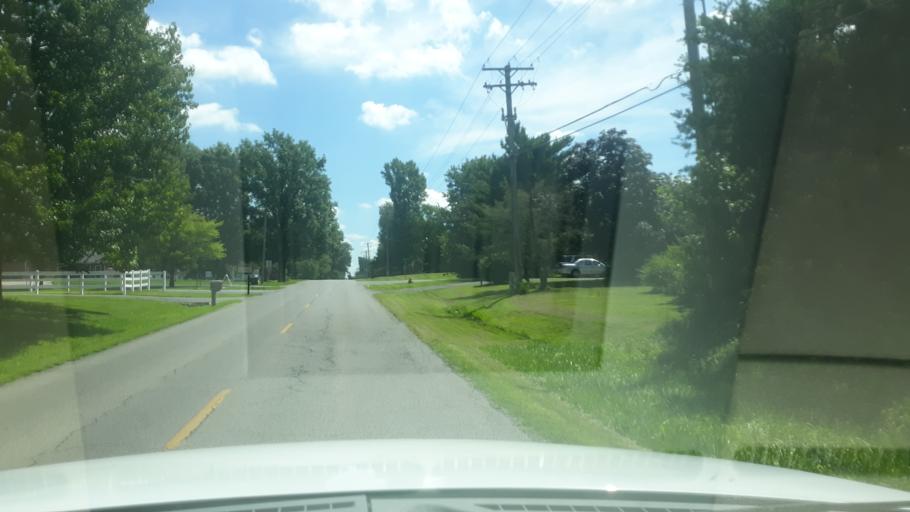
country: US
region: Illinois
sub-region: Saline County
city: Harrisburg
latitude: 37.7277
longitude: -88.5655
